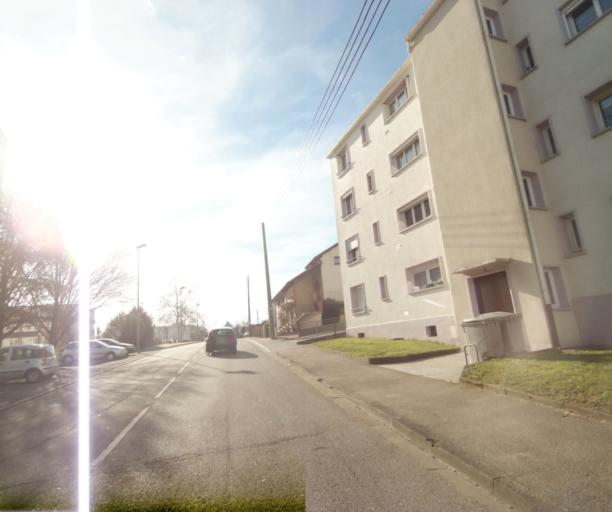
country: FR
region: Lorraine
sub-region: Departement de Meurthe-et-Moselle
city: Vandoeuvre-les-Nancy
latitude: 48.6604
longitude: 6.1696
